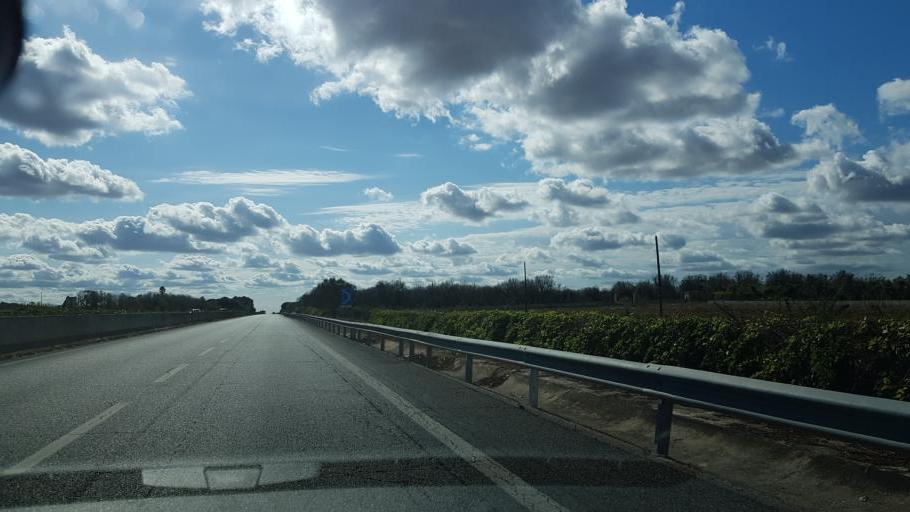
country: IT
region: Apulia
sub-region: Provincia di Brindisi
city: Torchiarolo
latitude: 40.4837
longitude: 18.0425
